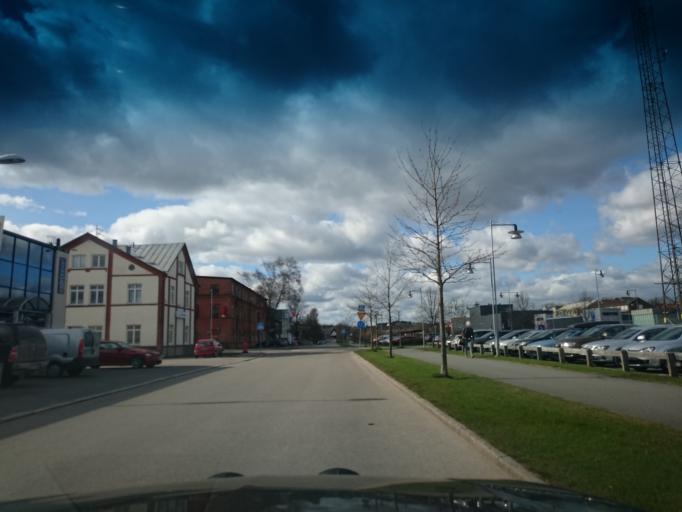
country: SE
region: Joenkoeping
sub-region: Vetlanda Kommun
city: Vetlanda
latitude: 57.4241
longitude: 15.0842
